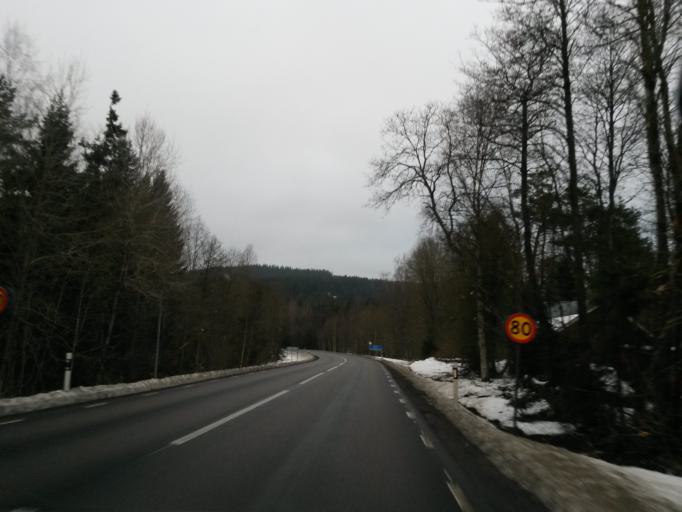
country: SE
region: Vaestra Goetaland
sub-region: Boras Kommun
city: Sandared
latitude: 57.8106
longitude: 12.7524
